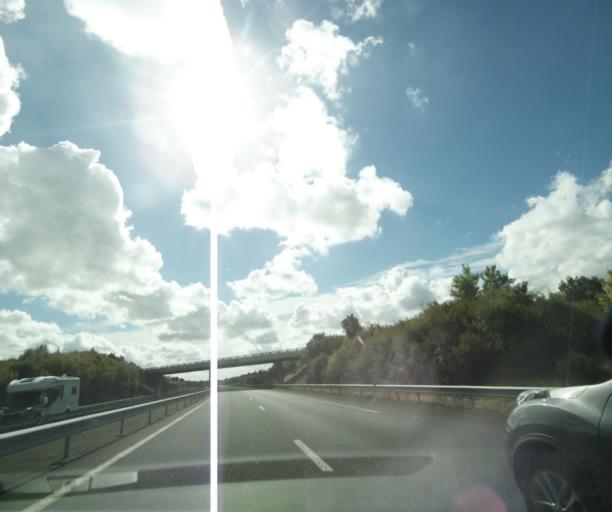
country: FR
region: Poitou-Charentes
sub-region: Departement de la Charente-Maritime
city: Saint-Savinien
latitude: 45.8548
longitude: -0.7265
